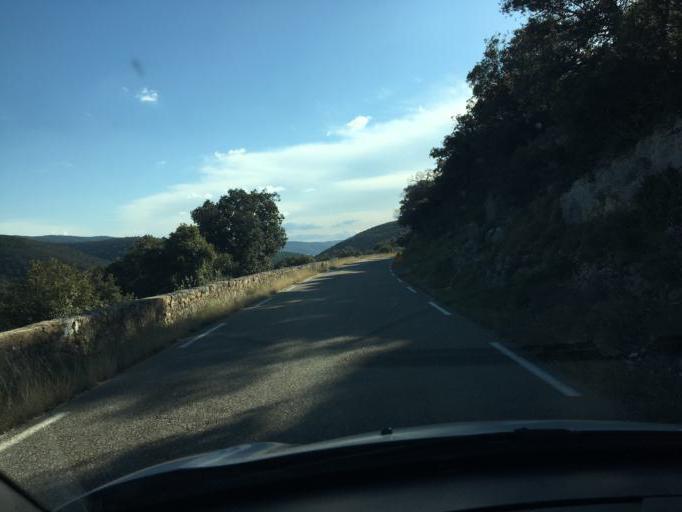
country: FR
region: Provence-Alpes-Cote d'Azur
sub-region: Departement du Vaucluse
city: Villes-sur-Auzon
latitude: 44.0450
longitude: 5.2755
